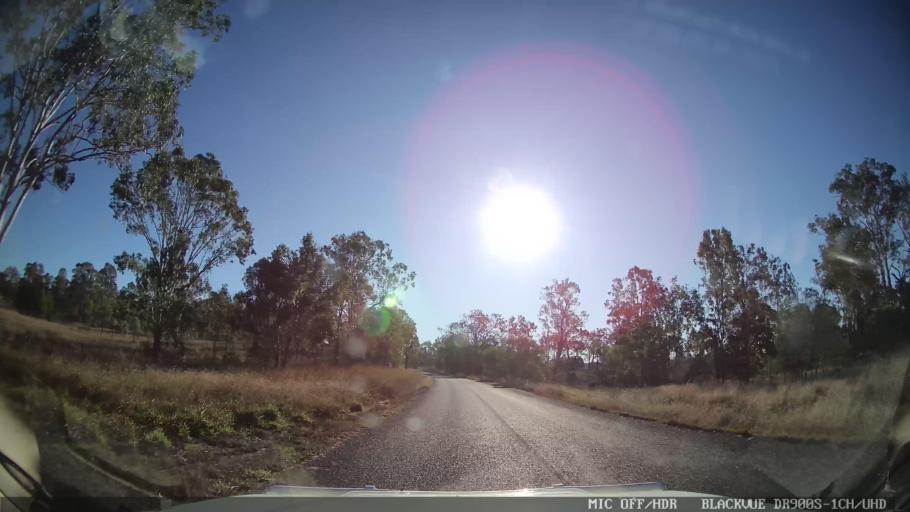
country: AU
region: Queensland
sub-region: Bundaberg
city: Sharon
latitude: -24.8045
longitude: 151.6525
